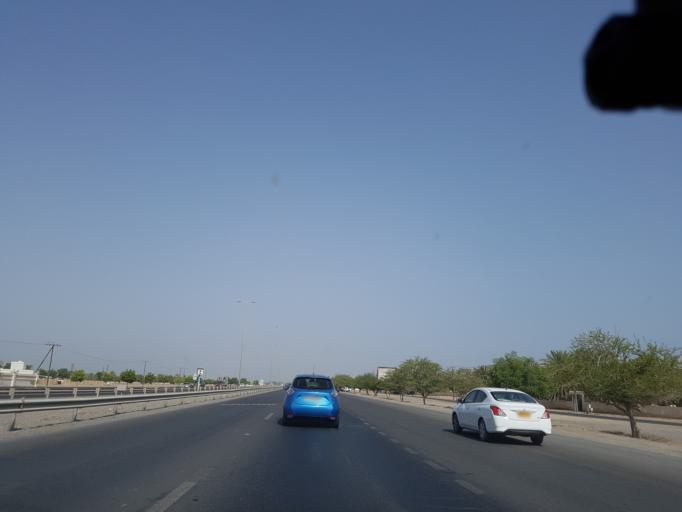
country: OM
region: Al Batinah
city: Barka'
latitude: 23.7223
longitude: 57.7334
